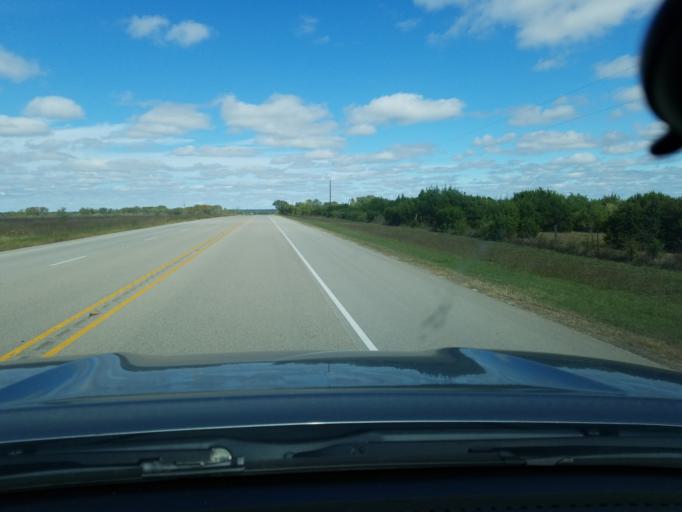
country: US
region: Texas
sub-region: Hamilton County
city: Hamilton
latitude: 31.5701
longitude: -98.1583
